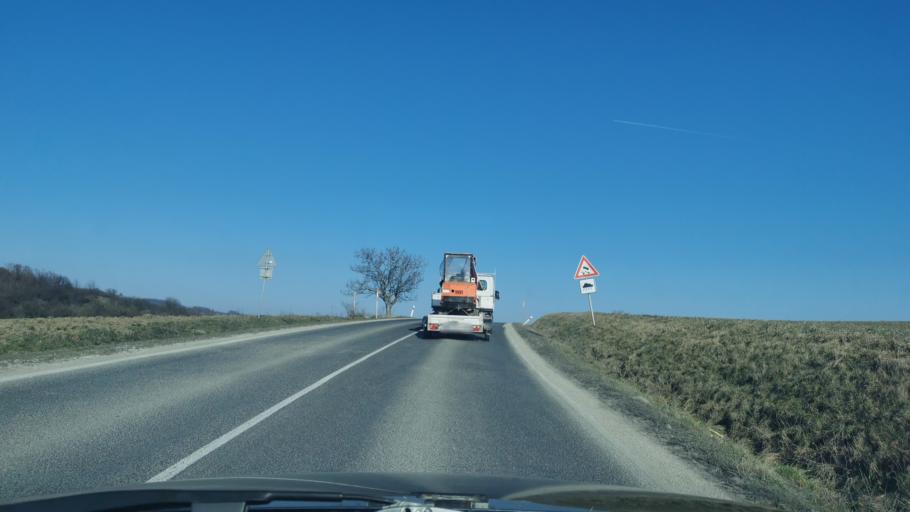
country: SK
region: Trnavsky
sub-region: Okres Senica
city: Senica
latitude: 48.7334
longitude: 17.4235
